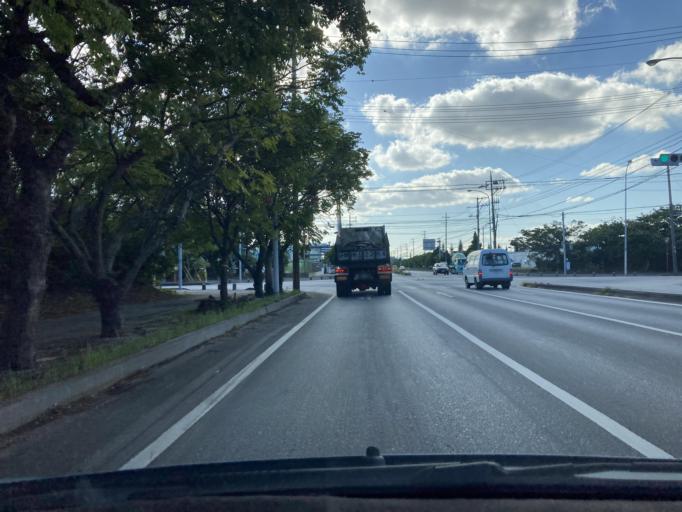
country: JP
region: Okinawa
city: Katsuren-haebaru
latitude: 26.3356
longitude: 127.8502
